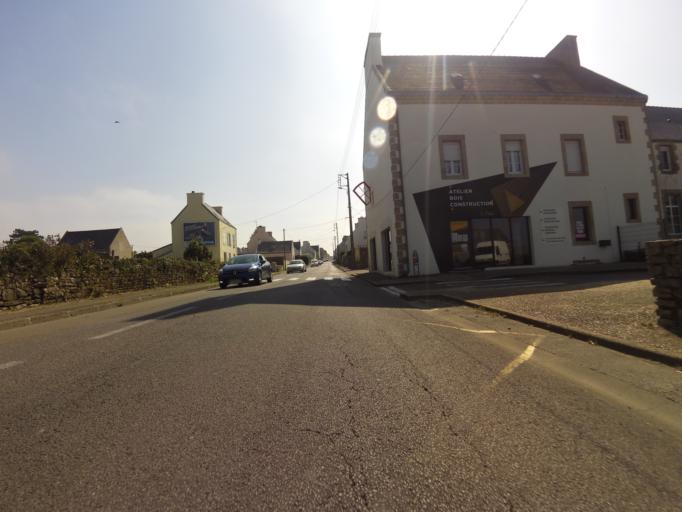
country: FR
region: Brittany
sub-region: Departement du Finistere
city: Plouhinec
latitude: 48.0154
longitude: -4.4945
